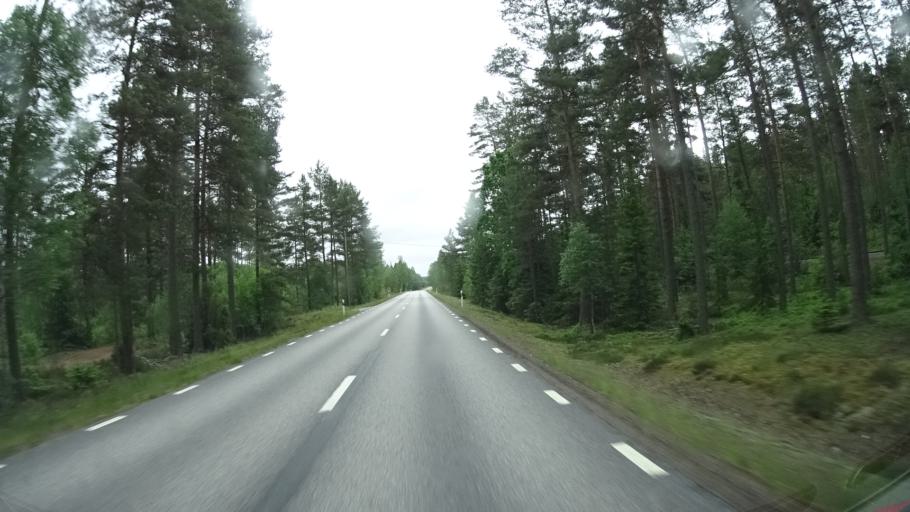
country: SE
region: Joenkoeping
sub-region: Eksjo Kommun
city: Mariannelund
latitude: 57.5615
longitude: 15.7092
